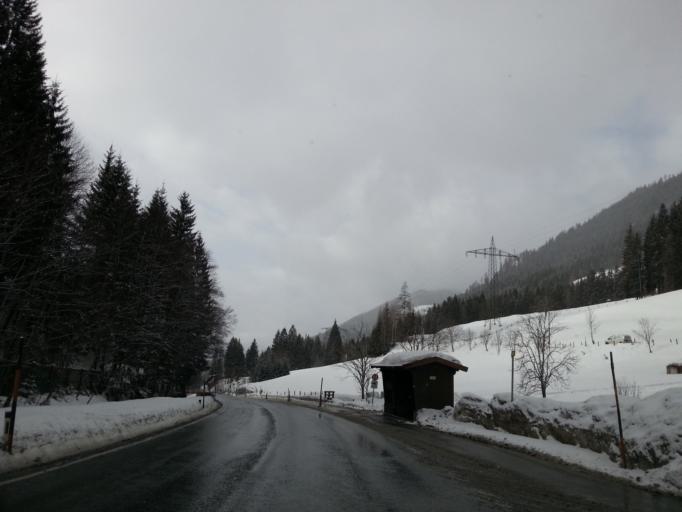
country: AT
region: Salzburg
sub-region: Politischer Bezirk Sankt Johann im Pongau
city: Eben im Pongau
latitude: 47.4563
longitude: 13.3706
